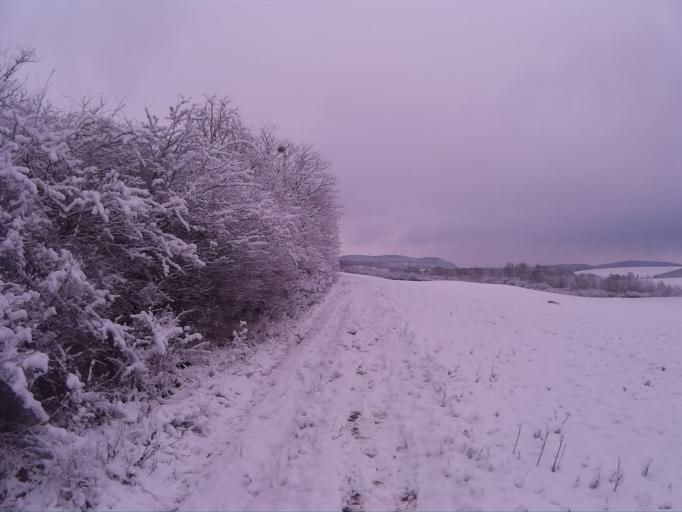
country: HU
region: Fejer
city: Szarliget
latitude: 47.5403
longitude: 18.5344
